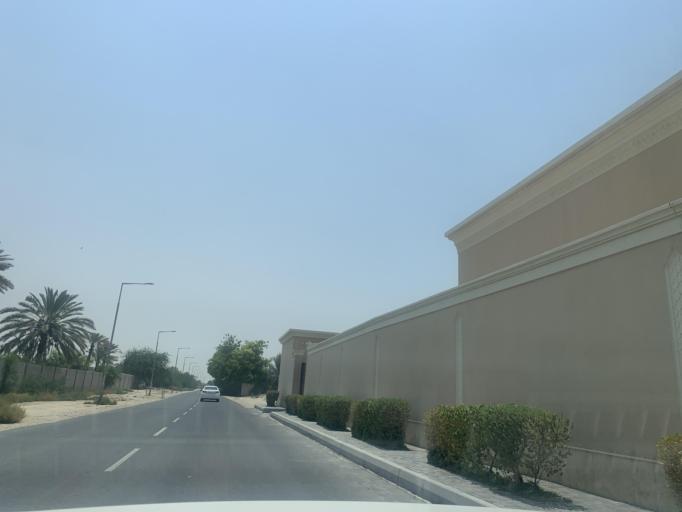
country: BH
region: Central Governorate
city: Madinat Hamad
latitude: 26.1495
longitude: 50.4653
